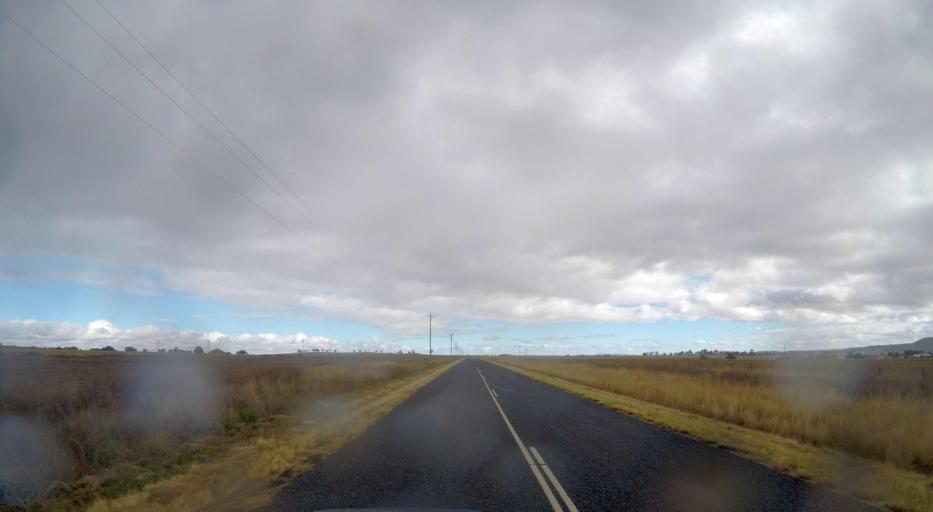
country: AU
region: Queensland
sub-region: Southern Downs
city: Warwick
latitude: -28.0530
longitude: 152.0289
